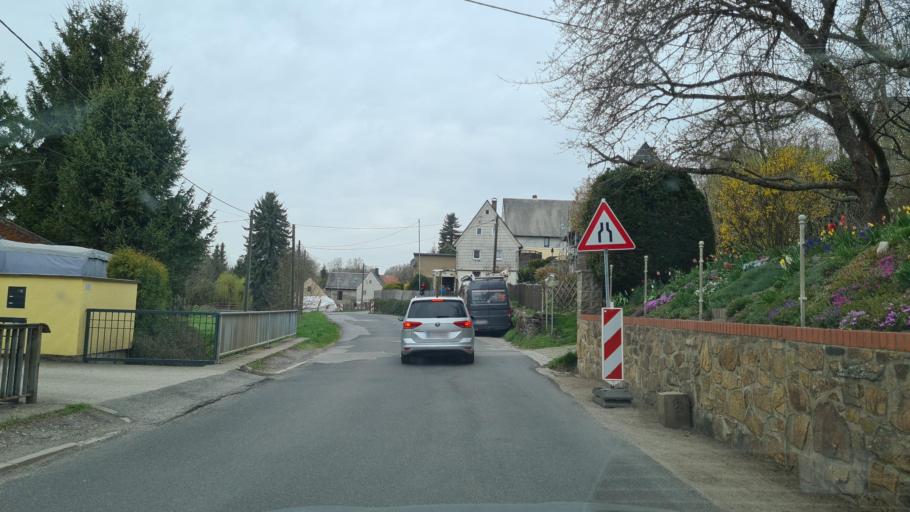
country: DE
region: Saxony
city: Claussnitz
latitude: 50.9024
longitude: 12.9103
